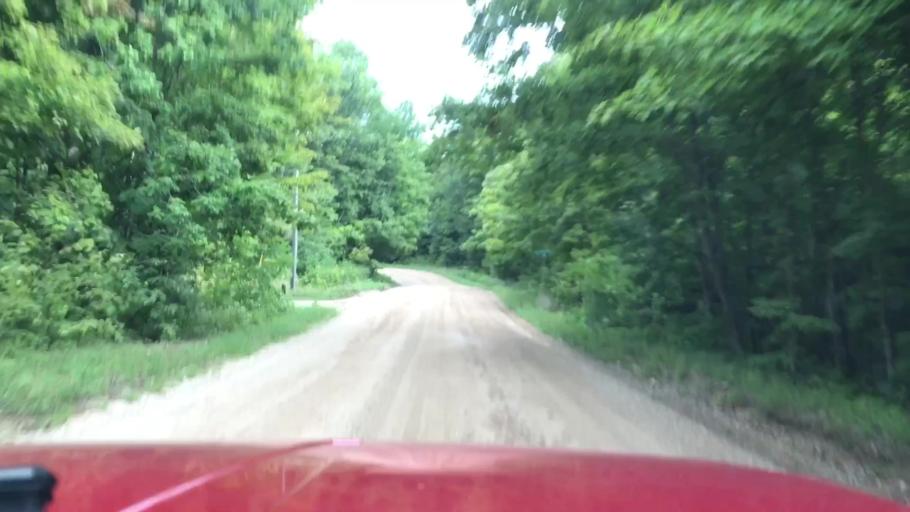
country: US
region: Michigan
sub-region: Charlevoix County
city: Charlevoix
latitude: 45.7348
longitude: -85.5579
